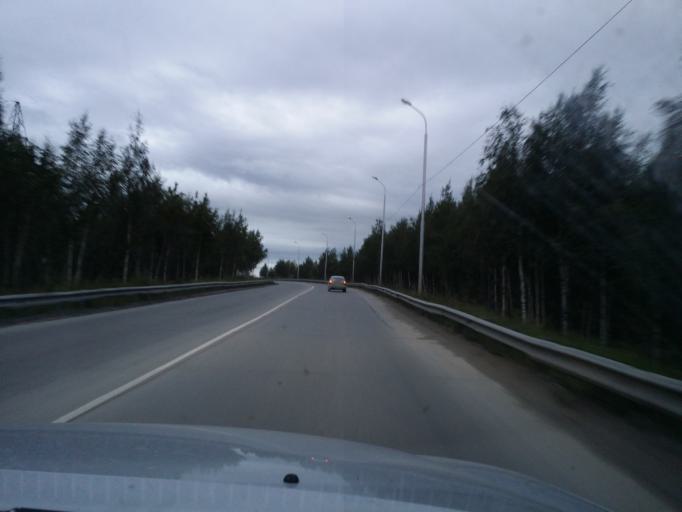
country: RU
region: Khanty-Mansiyskiy Avtonomnyy Okrug
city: Nizhnevartovsk
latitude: 60.9545
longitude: 76.6635
